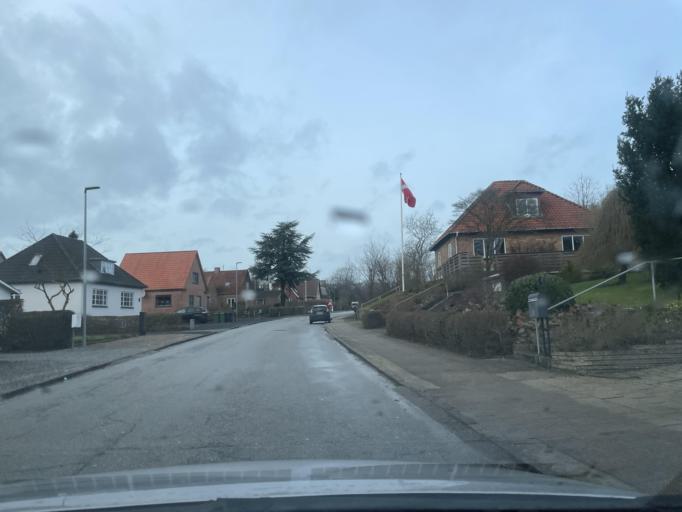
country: DK
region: South Denmark
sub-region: Haderslev Kommune
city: Haderslev
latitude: 55.2526
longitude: 9.4668
